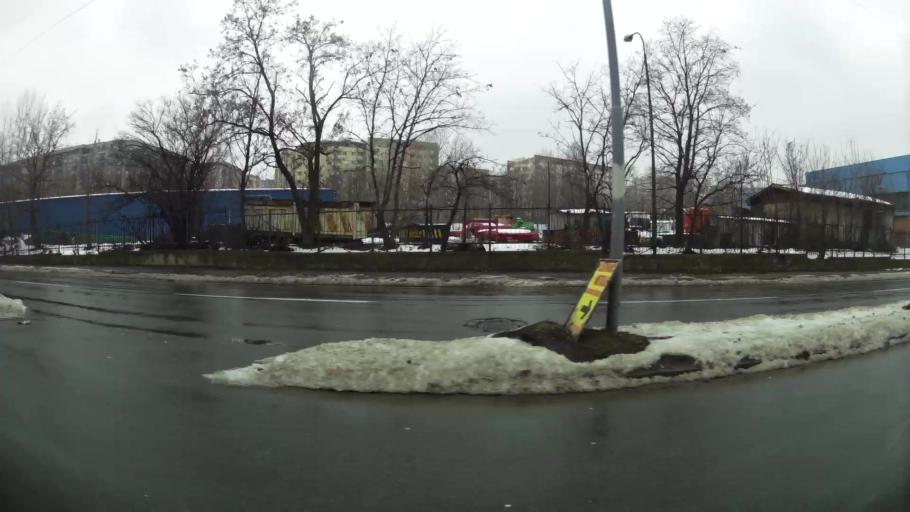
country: RS
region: Central Serbia
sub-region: Belgrade
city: Vozdovac
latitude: 44.7620
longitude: 20.4912
